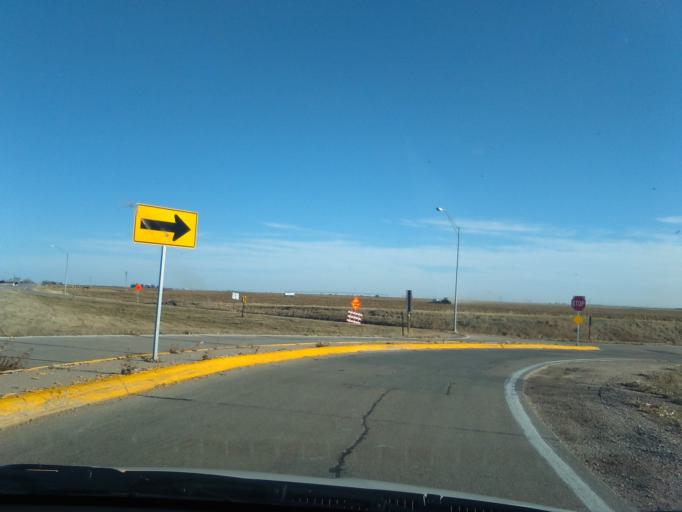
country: US
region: Nebraska
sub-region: Adams County
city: Hastings
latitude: 40.4373
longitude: -98.4343
